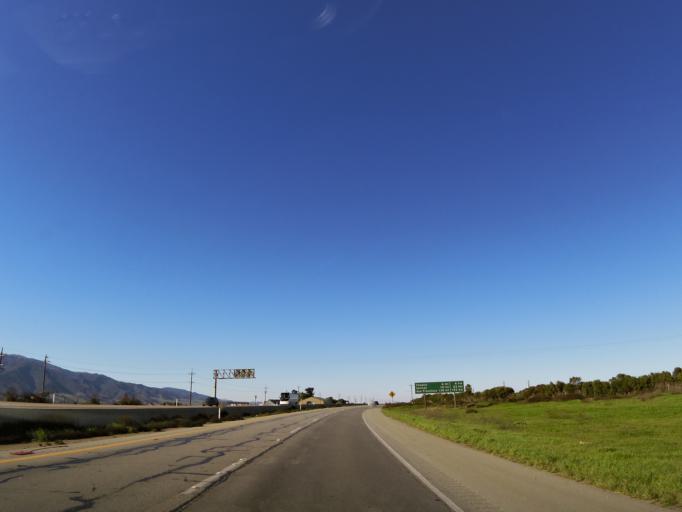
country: US
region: California
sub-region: Monterey County
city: Gonzales
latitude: 36.5248
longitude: -121.4666
